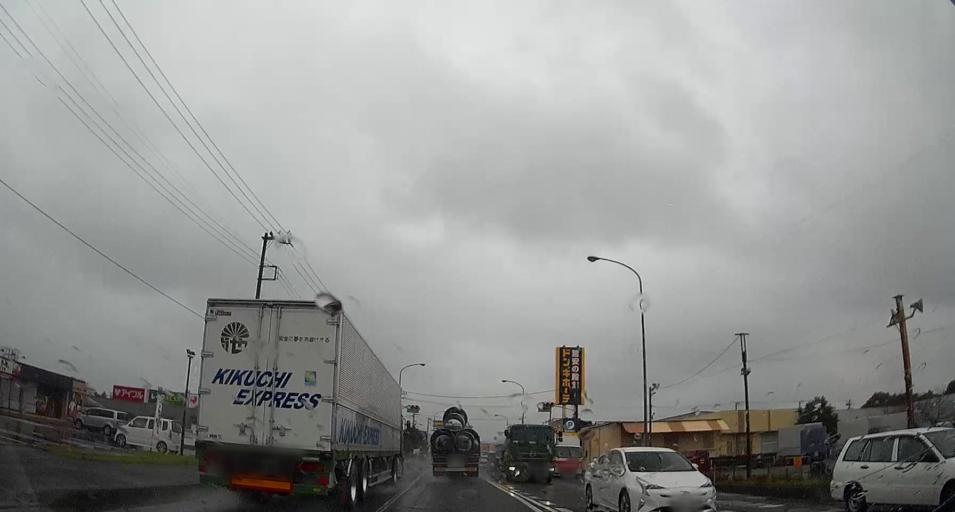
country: JP
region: Chiba
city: Chiba
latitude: 35.5524
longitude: 140.1250
